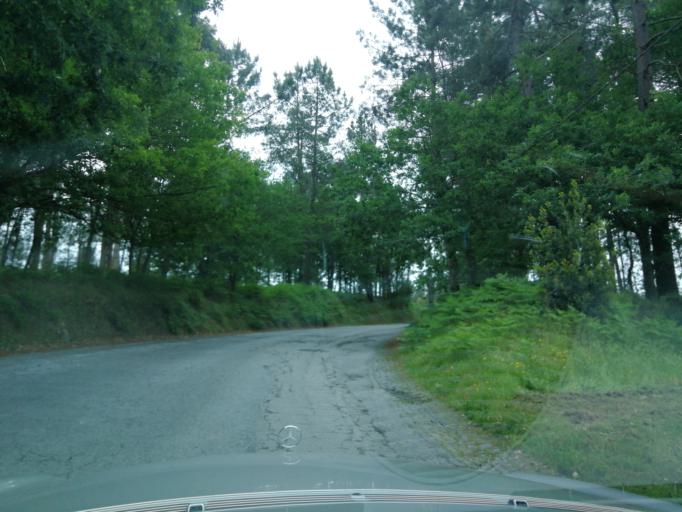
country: PT
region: Braga
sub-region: Braga
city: Adaufe
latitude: 41.6042
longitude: -8.4009
